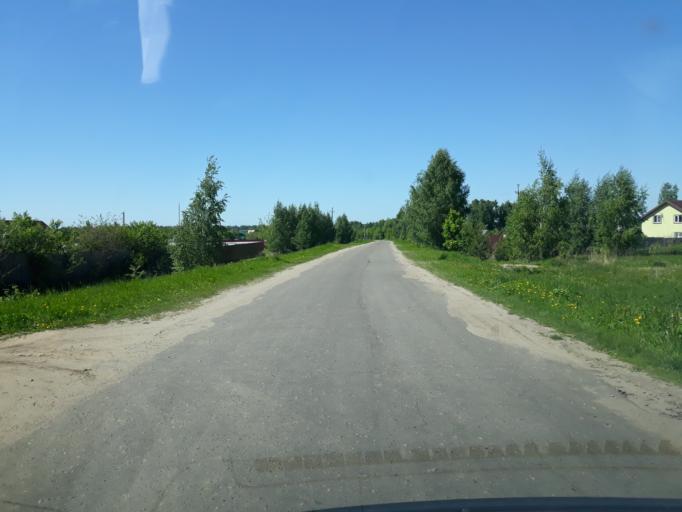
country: RU
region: Jaroslavl
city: Yaroslavl
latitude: 57.6734
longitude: 40.0261
